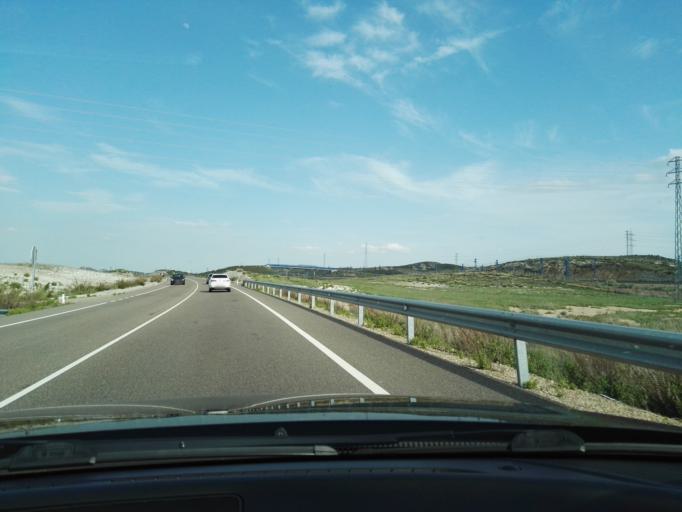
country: ES
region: Aragon
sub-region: Provincia de Zaragoza
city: Montecanal
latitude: 41.6226
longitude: -0.9814
